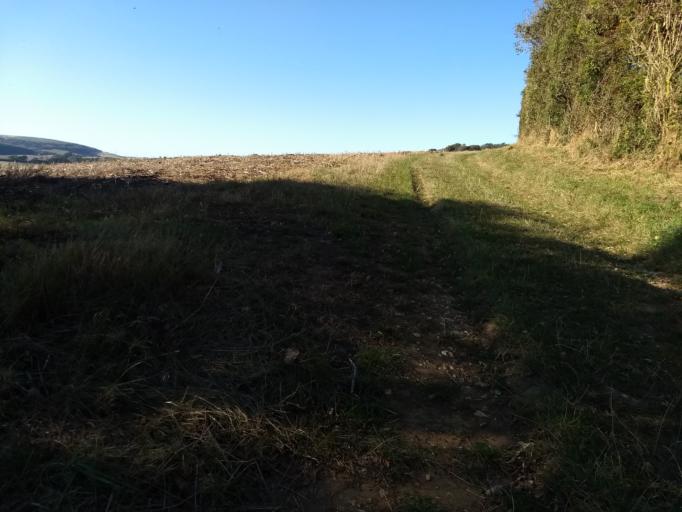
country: GB
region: England
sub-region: Isle of Wight
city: Newport
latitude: 50.6496
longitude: -1.2878
